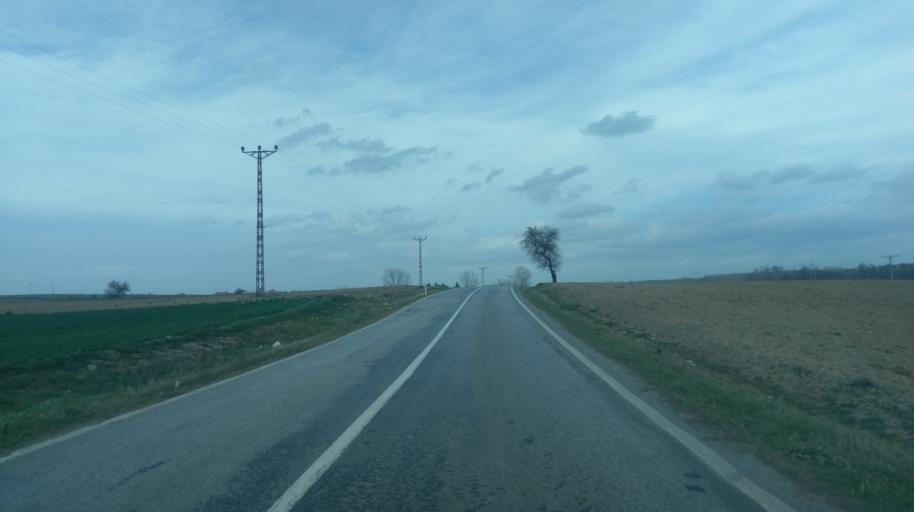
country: TR
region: Edirne
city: Havsa
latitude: 41.5739
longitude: 26.8321
